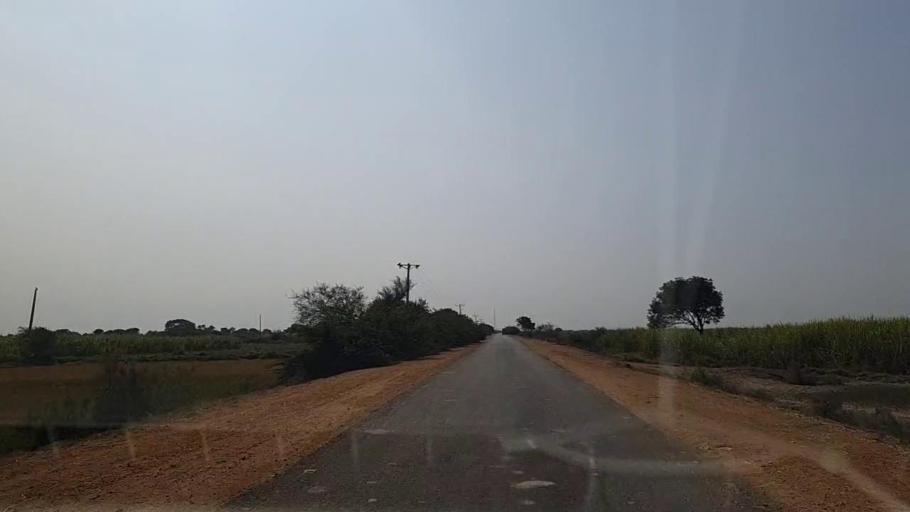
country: PK
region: Sindh
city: Chuhar Jamali
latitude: 24.2977
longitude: 67.9310
